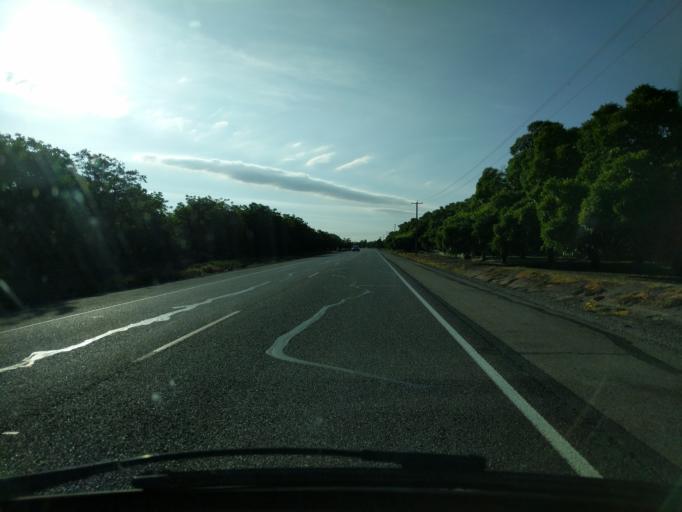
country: US
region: California
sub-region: San Joaquin County
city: Garden Acres
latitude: 37.9461
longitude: -121.1585
